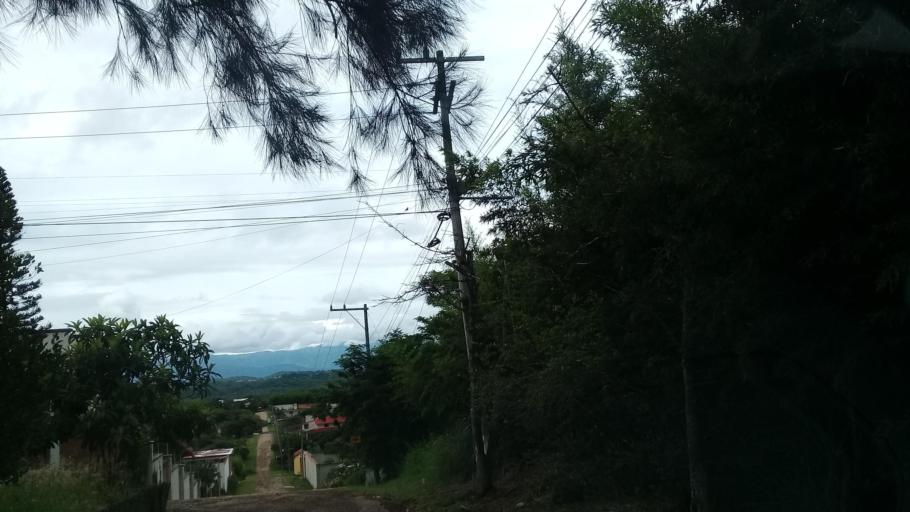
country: MX
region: Veracruz
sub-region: Emiliano Zapata
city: Jacarandas
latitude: 19.5058
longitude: -96.8498
